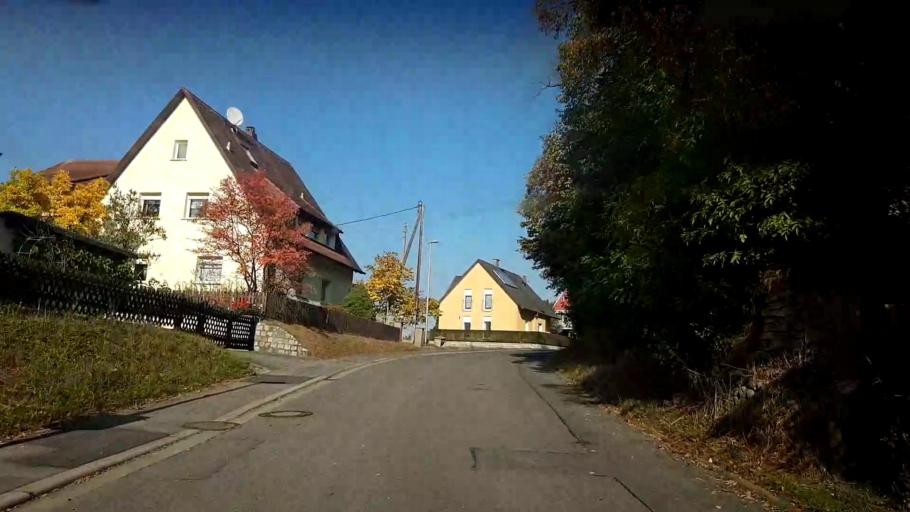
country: DE
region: Bavaria
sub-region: Upper Franconia
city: Stegaurach
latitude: 49.8717
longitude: 10.8151
